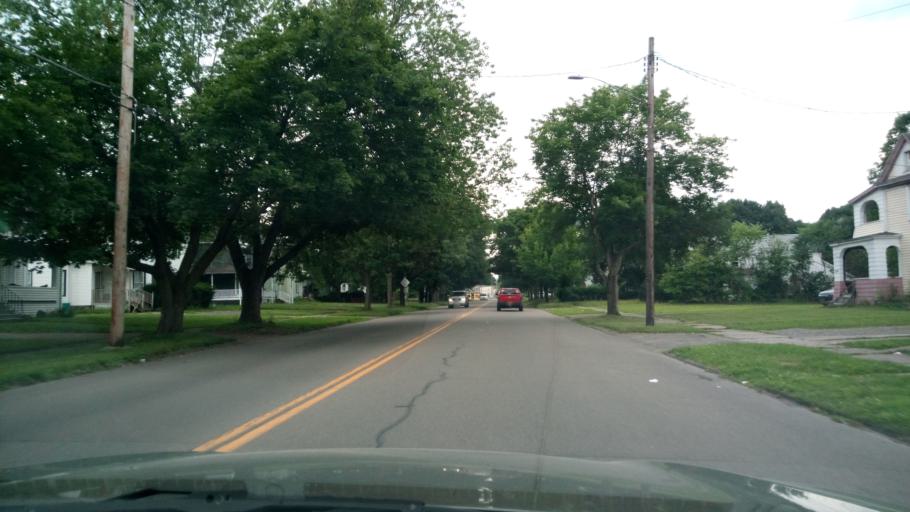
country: US
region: New York
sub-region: Chemung County
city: Elmira
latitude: 42.1109
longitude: -76.8068
